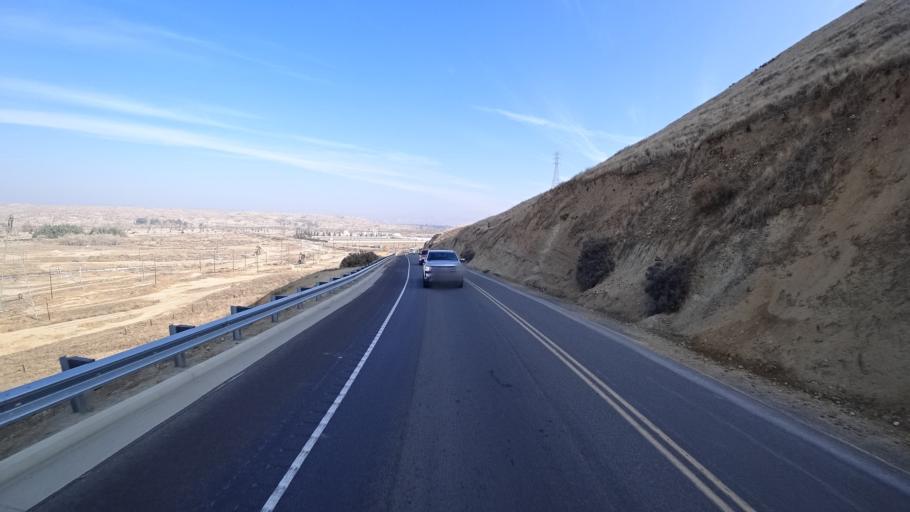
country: US
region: California
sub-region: Kern County
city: Oildale
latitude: 35.4134
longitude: -118.9701
